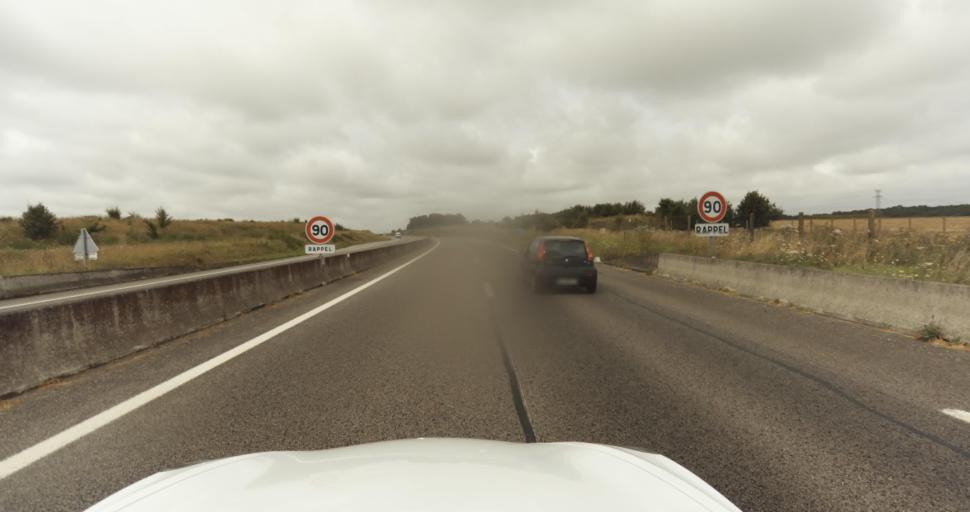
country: FR
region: Haute-Normandie
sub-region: Departement de l'Eure
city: Aviron
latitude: 49.0365
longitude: 1.1021
